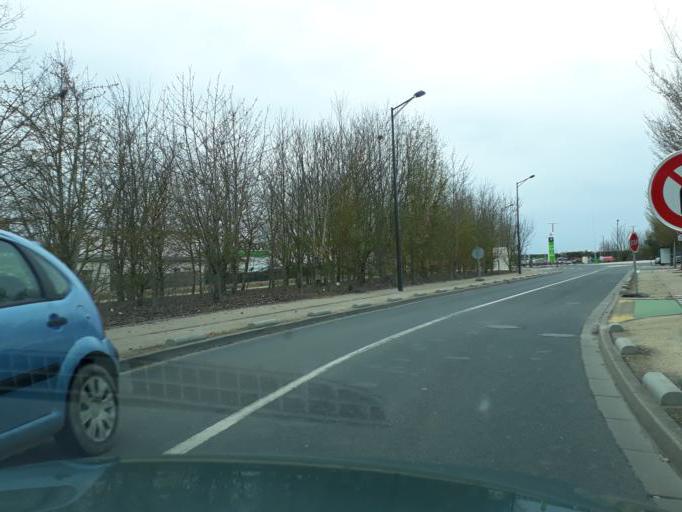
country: FR
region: Centre
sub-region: Departement du Loir-et-Cher
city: Villebarou
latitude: 47.6142
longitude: 1.3238
